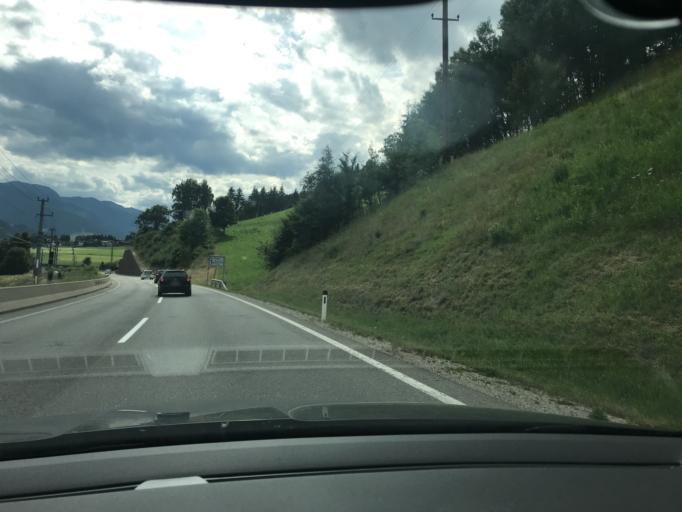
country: AT
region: Tyrol
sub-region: Politischer Bezirk Lienz
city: Abfaltersbach
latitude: 46.7579
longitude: 12.5172
